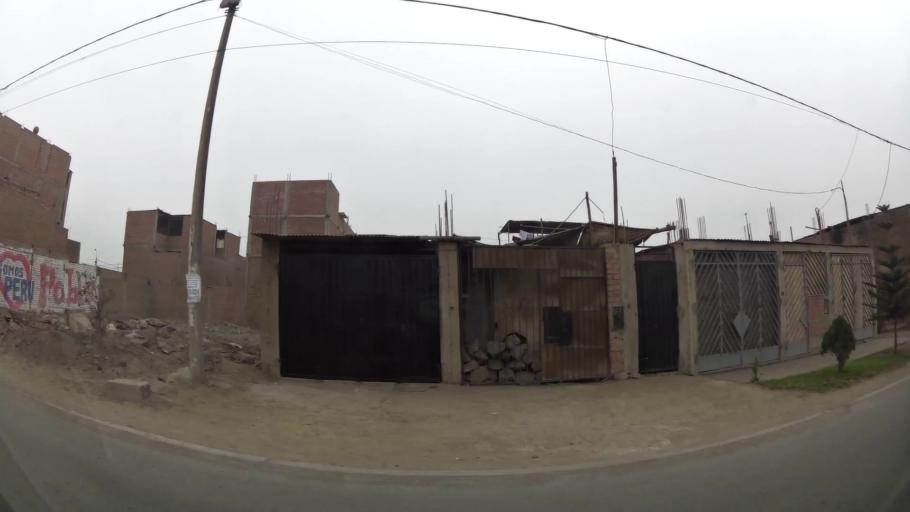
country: PE
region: Lima
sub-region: Lima
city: Urb. Santo Domingo
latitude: -11.8713
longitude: -77.0273
